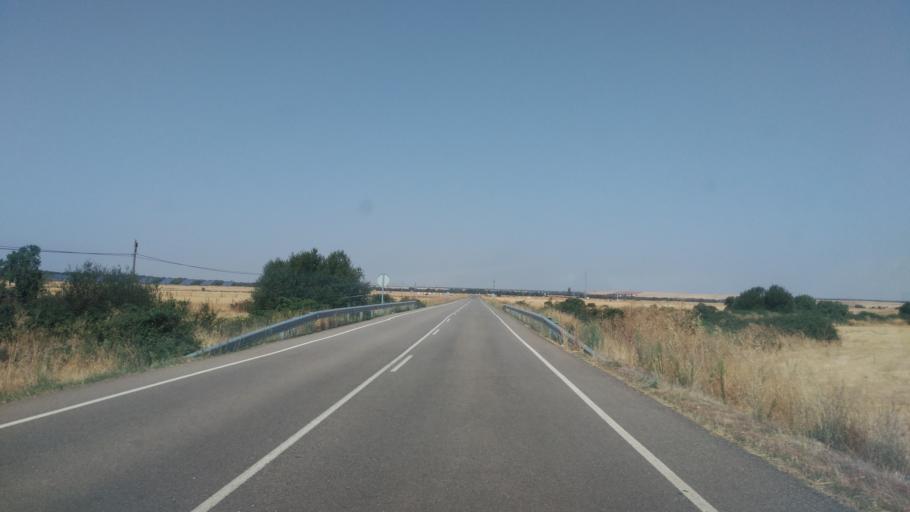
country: ES
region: Castille and Leon
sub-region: Provincia de Salamanca
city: Abusejo
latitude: 40.7129
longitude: -6.1440
